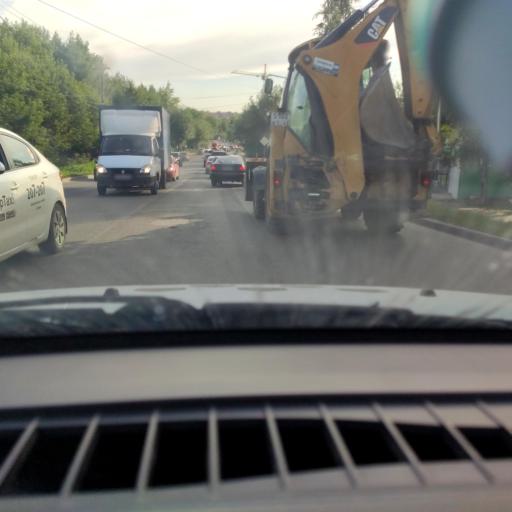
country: RU
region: Kirov
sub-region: Kirovo-Chepetskiy Rayon
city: Kirov
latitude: 58.6223
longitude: 49.6382
